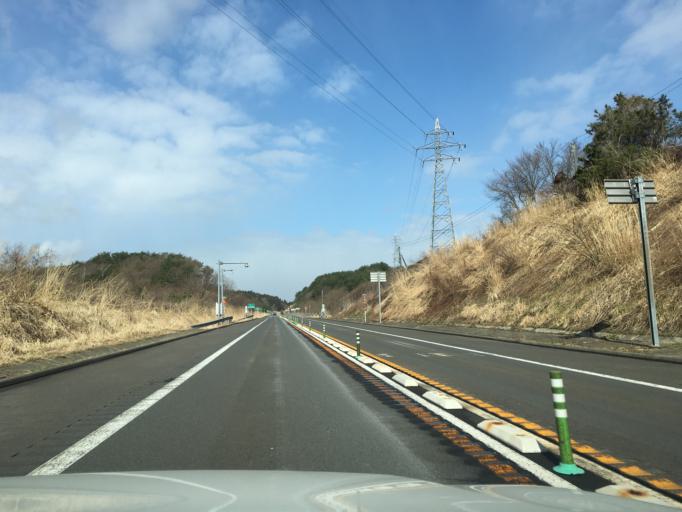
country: JP
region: Akita
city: Akita
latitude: 39.7585
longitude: 140.1334
